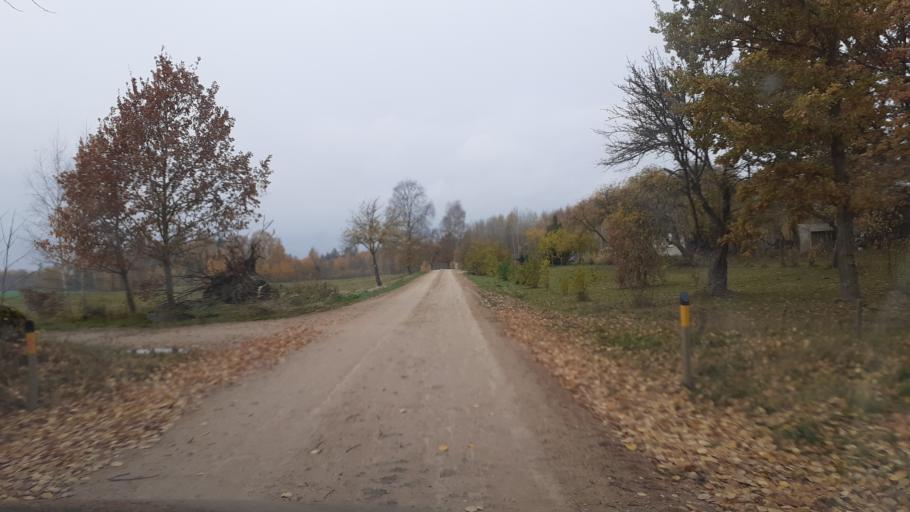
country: LV
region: Saldus Rajons
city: Saldus
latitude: 56.8743
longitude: 22.3196
